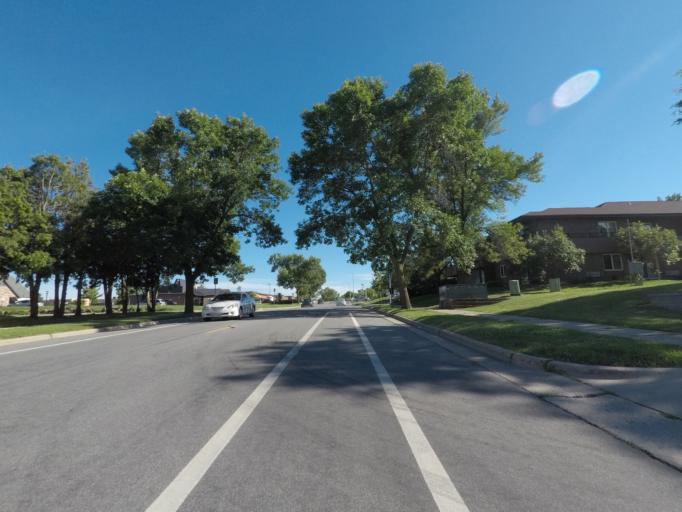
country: US
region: Wisconsin
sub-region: Dane County
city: Middleton
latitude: 43.0619
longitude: -89.5127
